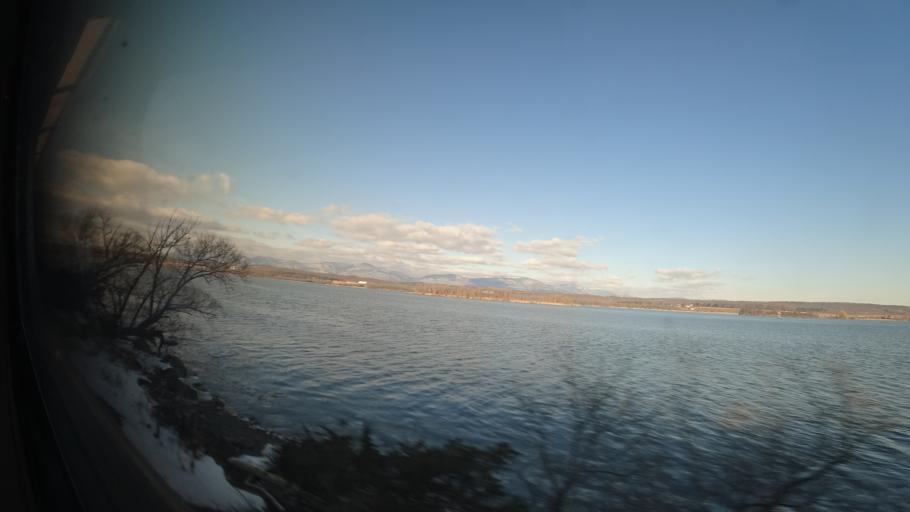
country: US
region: New York
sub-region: Greene County
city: Catskill
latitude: 42.1654
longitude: -73.8791
